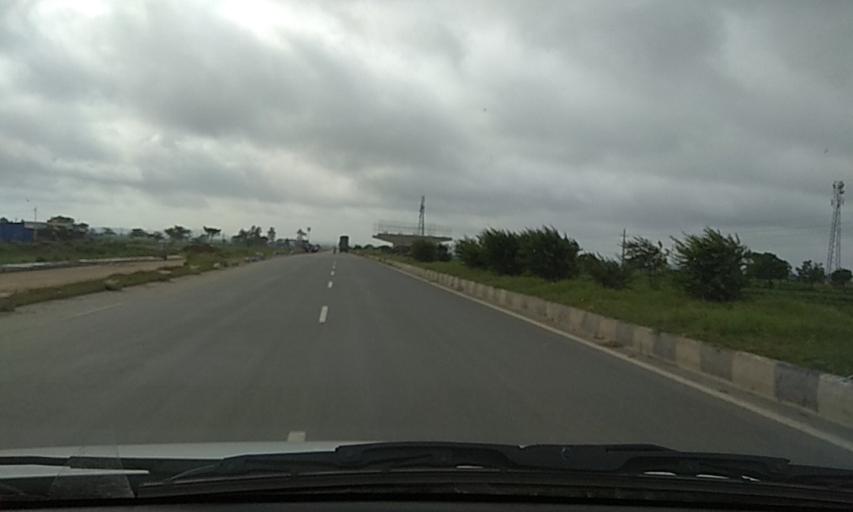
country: IN
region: Karnataka
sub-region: Haveri
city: Savanur
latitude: 14.8844
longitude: 75.3061
